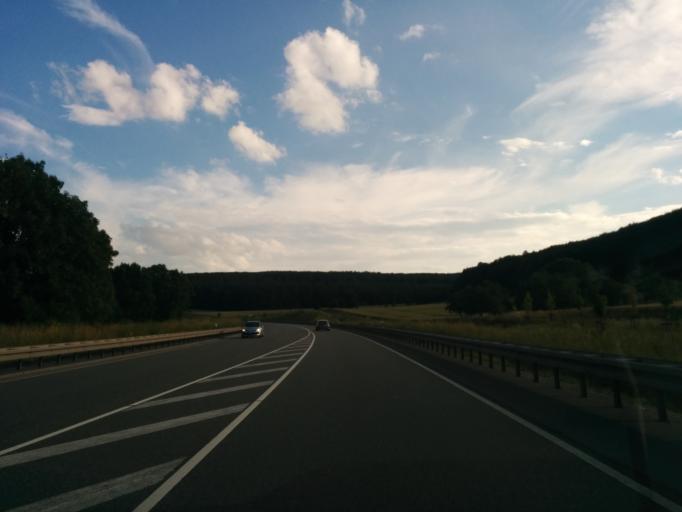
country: DE
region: Thuringia
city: Sondershausen
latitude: 51.3545
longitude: 10.8244
